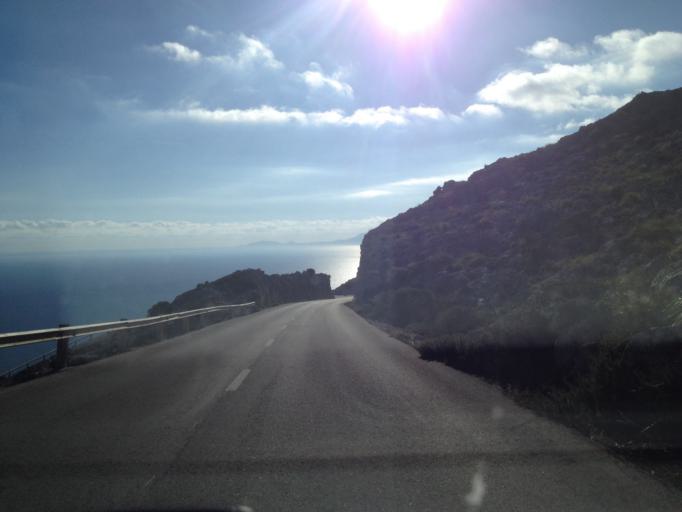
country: ES
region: Balearic Islands
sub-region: Illes Balears
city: Alcudia
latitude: 39.9563
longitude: 3.2108
